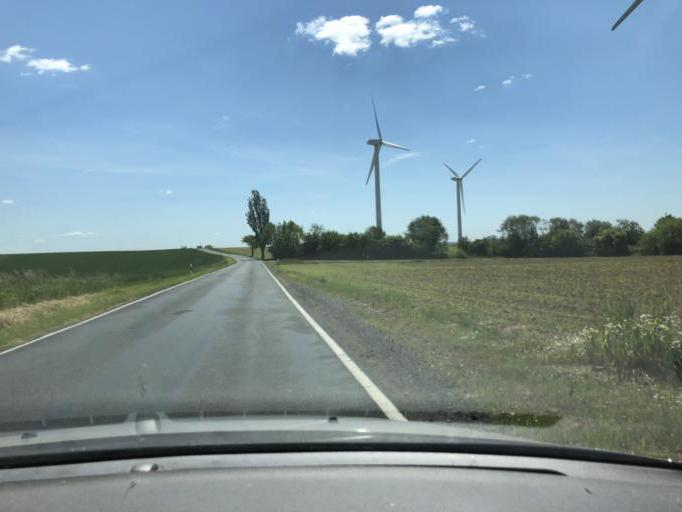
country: DE
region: Saxony
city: Nerchau
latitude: 51.2413
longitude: 12.8160
